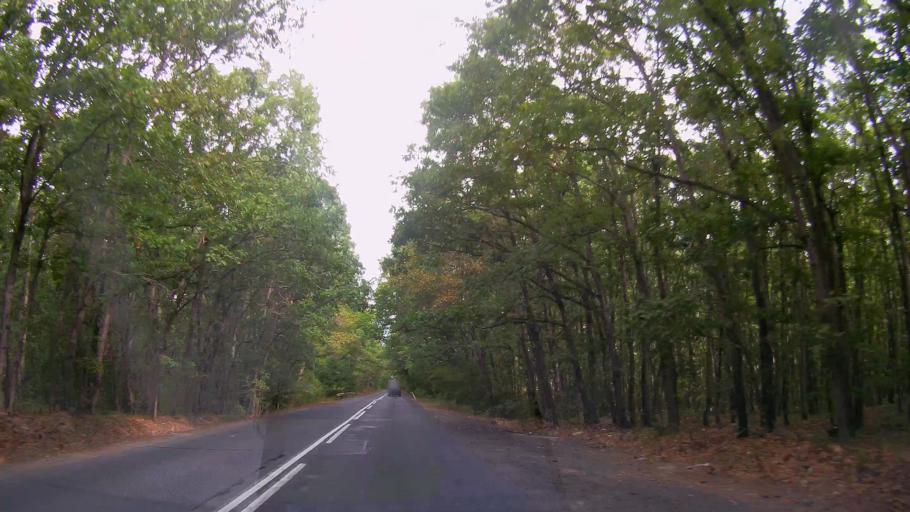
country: BG
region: Burgas
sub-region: Obshtina Primorsko
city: Primorsko
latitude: 42.2780
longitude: 27.7396
